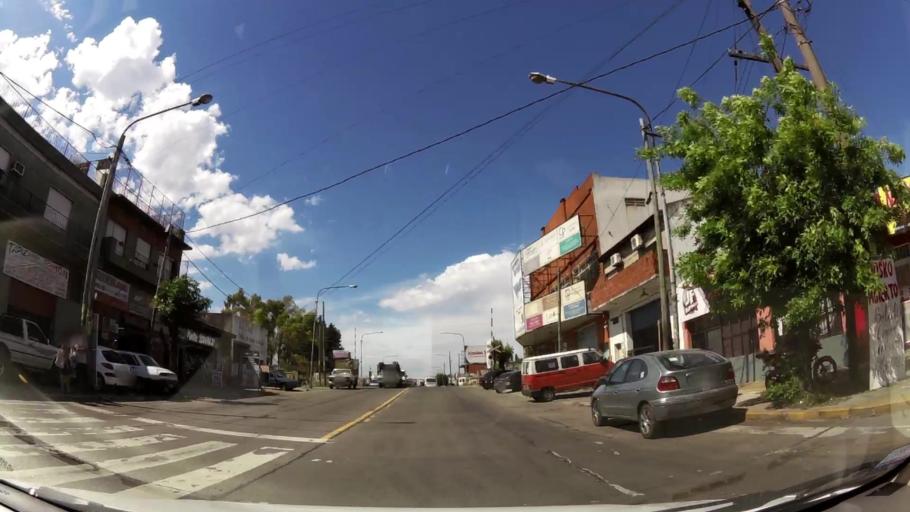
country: AR
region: Buenos Aires
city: San Justo
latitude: -34.6716
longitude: -58.5595
